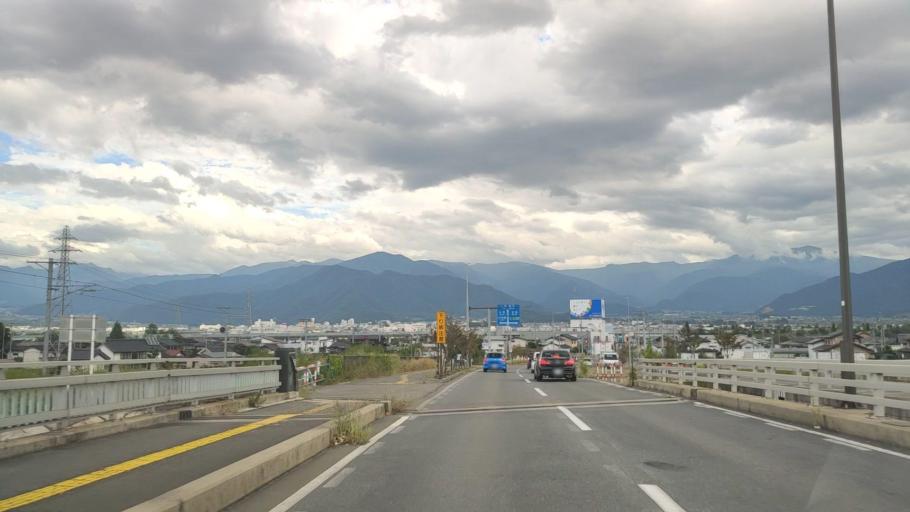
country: JP
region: Nagano
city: Suzaka
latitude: 36.6605
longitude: 138.2760
